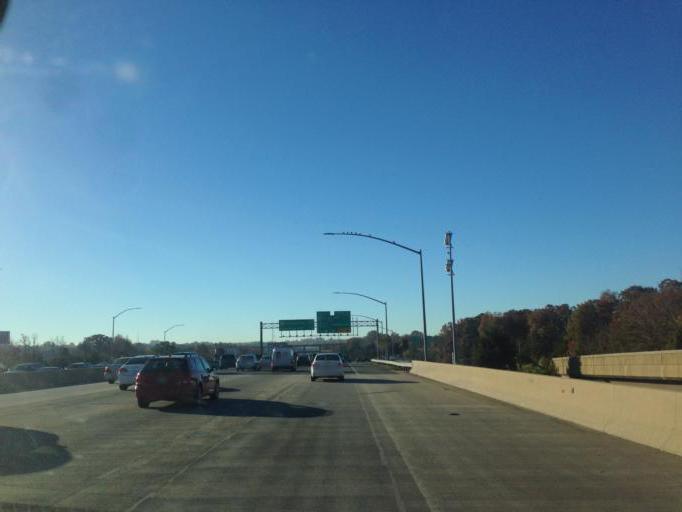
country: US
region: Maryland
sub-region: Baltimore County
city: Woodlawn
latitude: 39.3128
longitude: -76.7448
